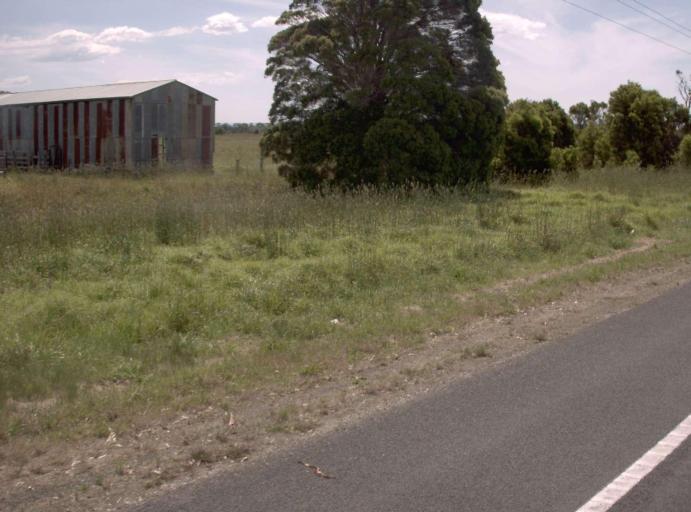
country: AU
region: Victoria
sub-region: Wellington
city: Sale
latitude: -38.0597
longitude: 147.0701
